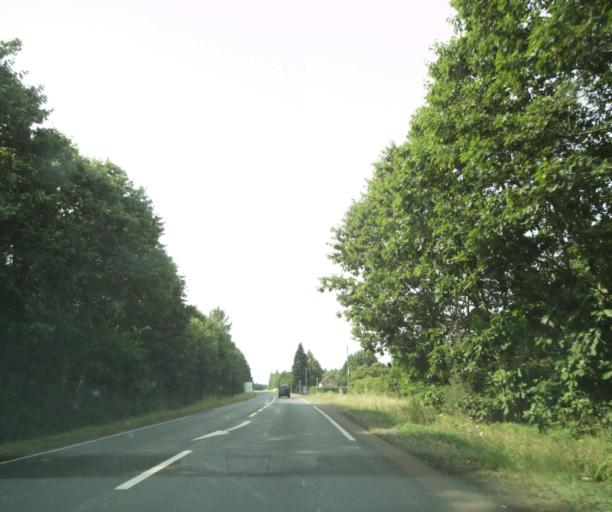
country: FR
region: Pays de la Loire
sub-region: Departement de la Sarthe
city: Marigne-Laille
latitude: 47.7760
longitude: 0.3446
